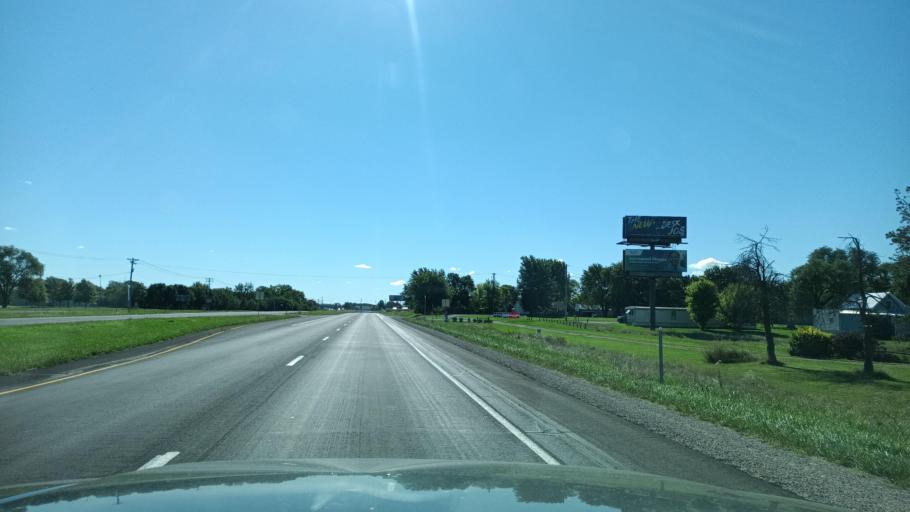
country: US
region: Iowa
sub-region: Lee County
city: Keokuk
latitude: 40.4417
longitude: -91.4346
